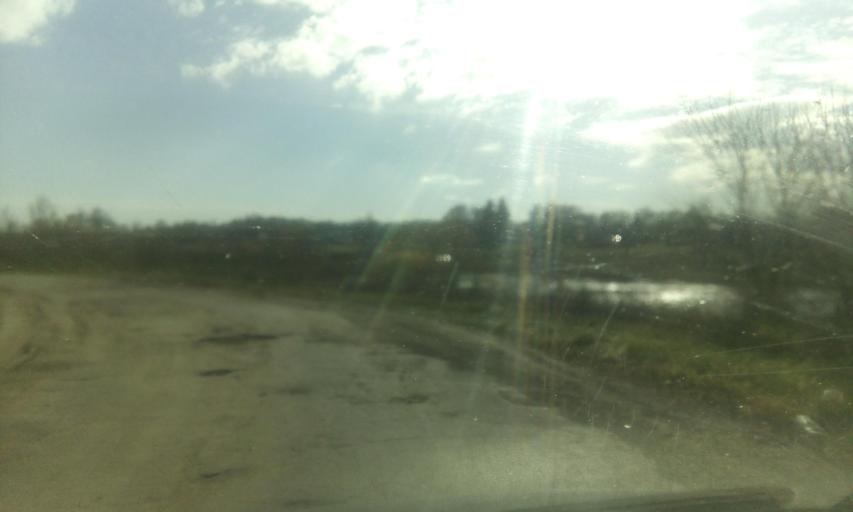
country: RU
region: Tula
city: Dubovka
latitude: 53.9492
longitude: 38.0276
